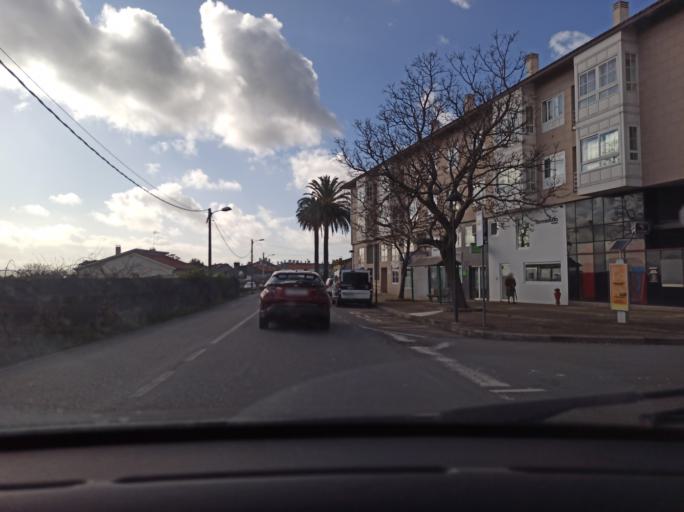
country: ES
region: Galicia
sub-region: Provincia da Coruna
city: Oleiros
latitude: 43.3328
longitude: -8.3184
